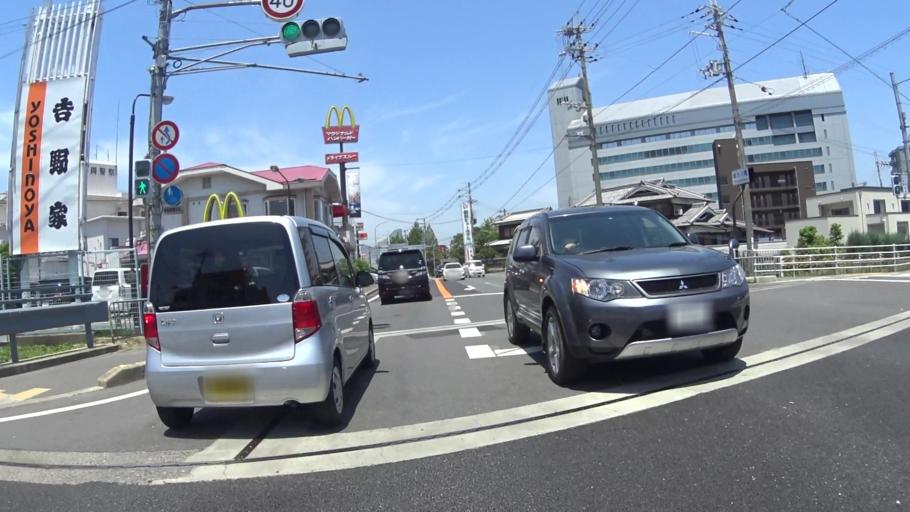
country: JP
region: Kyoto
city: Kameoka
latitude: 35.0121
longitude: 135.5738
